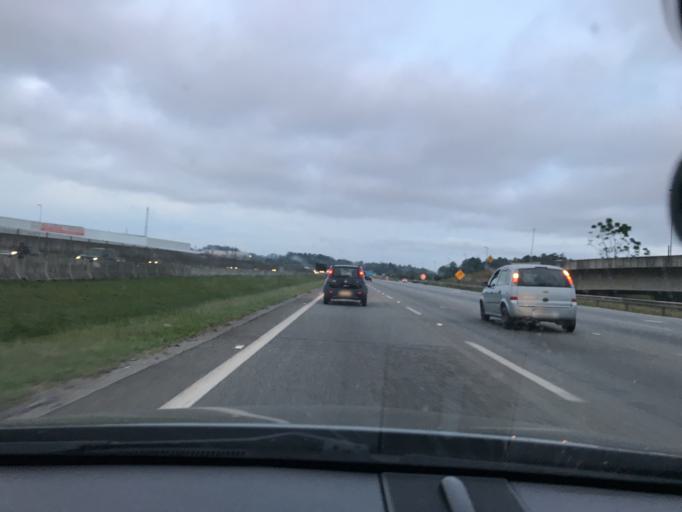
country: BR
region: Sao Paulo
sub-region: Guarulhos
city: Guarulhos
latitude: -23.4810
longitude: -46.4528
